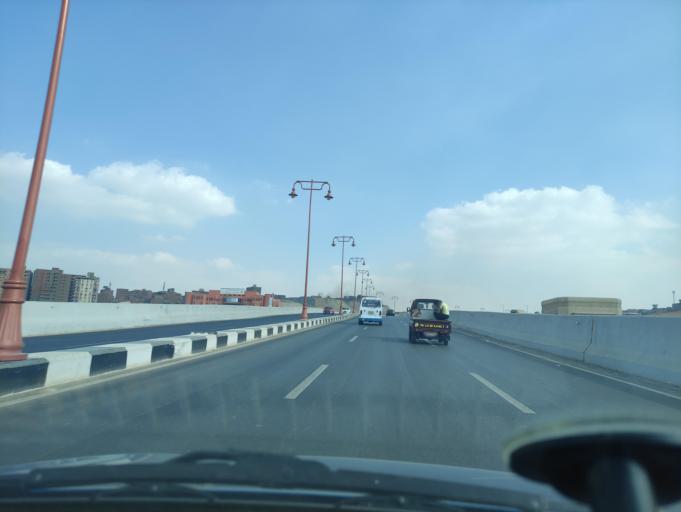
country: EG
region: Muhafazat al Qahirah
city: Cairo
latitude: 30.0510
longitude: 31.2849
